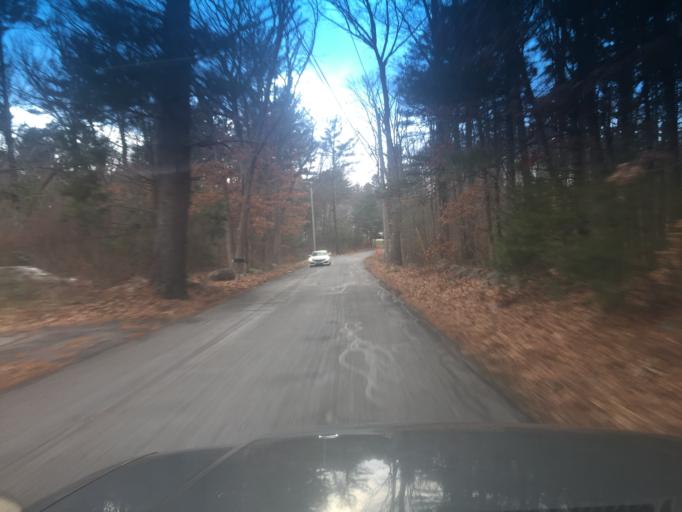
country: US
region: Massachusetts
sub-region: Norfolk County
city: Bellingham
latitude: 42.1183
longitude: -71.4422
